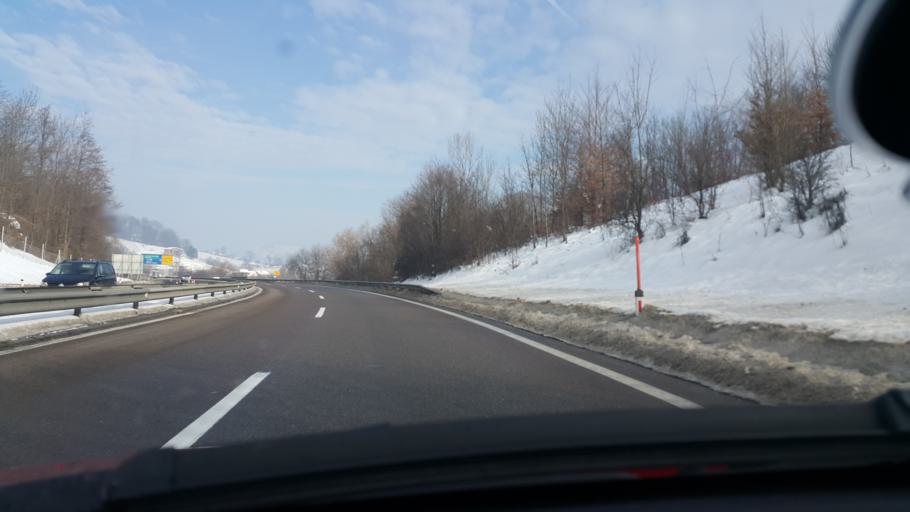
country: SI
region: Pesnica
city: Pesnica pri Mariboru
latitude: 46.5858
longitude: 15.6699
